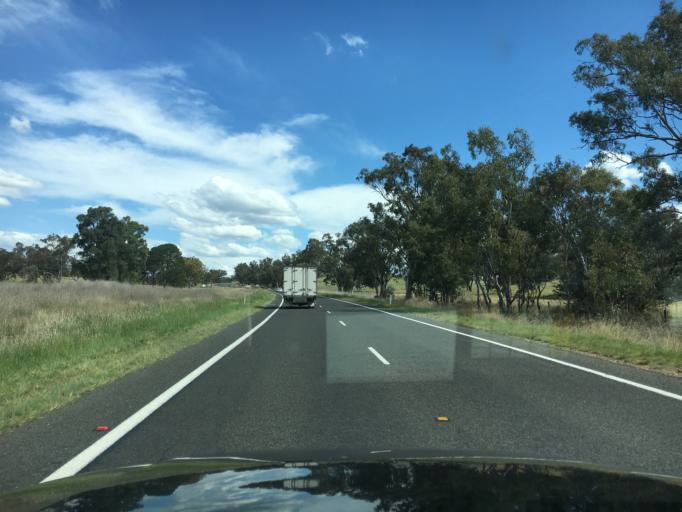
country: AU
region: New South Wales
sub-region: Liverpool Plains
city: Quirindi
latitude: -31.4887
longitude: 150.8640
